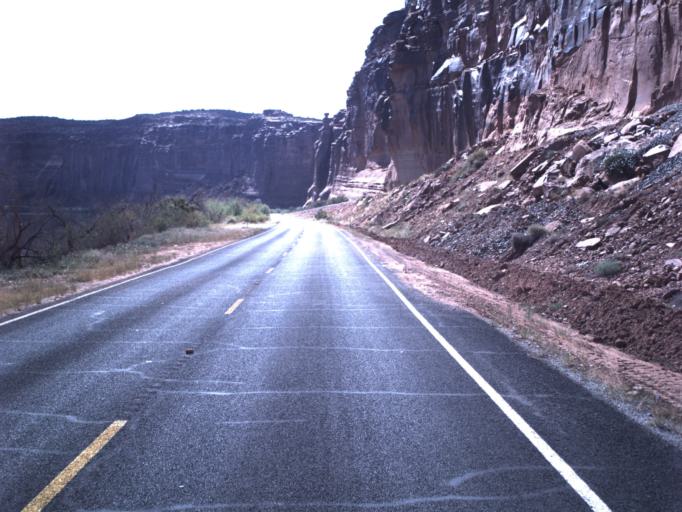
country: US
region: Utah
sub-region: Grand County
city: Moab
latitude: 38.5776
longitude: -109.6478
